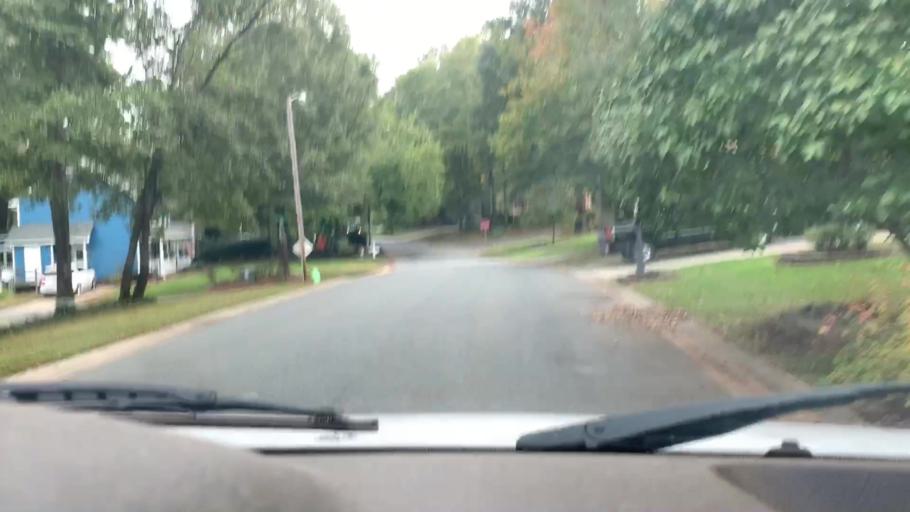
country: US
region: North Carolina
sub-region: Mecklenburg County
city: Cornelius
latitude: 35.4747
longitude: -80.8601
